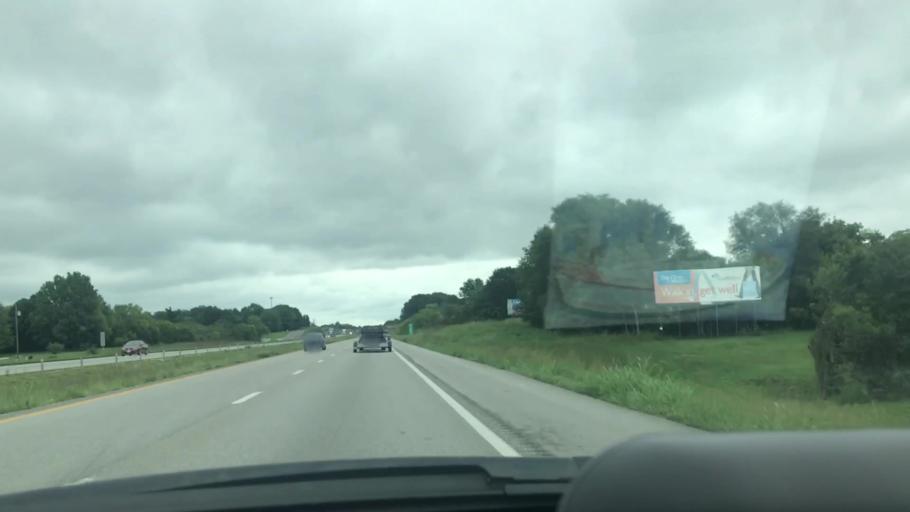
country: US
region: Missouri
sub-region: Greene County
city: Springfield
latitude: 37.2501
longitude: -93.3255
